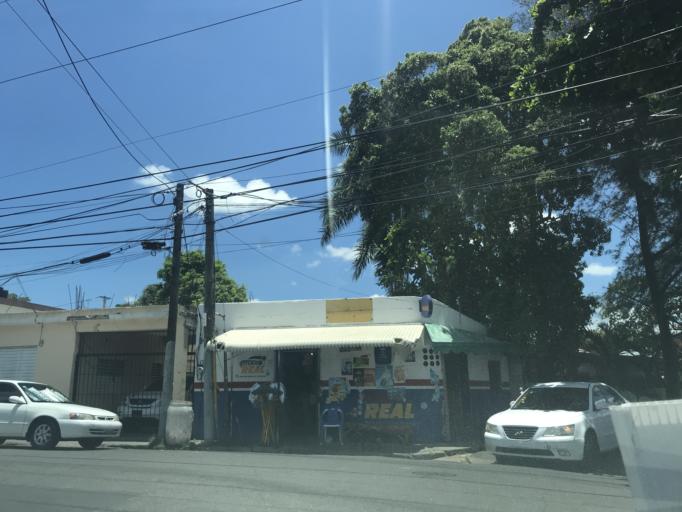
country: DO
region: Santiago
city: Santiago de los Caballeros
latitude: 19.4375
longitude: -70.6949
